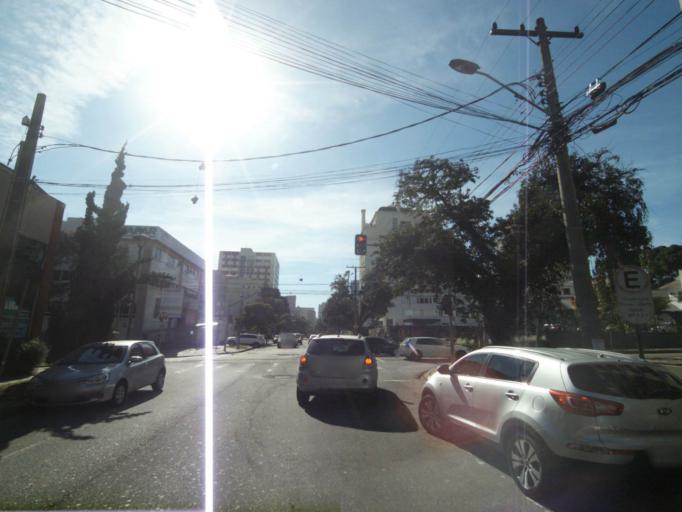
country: BR
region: Parana
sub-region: Curitiba
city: Curitiba
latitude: -25.4395
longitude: -49.2855
